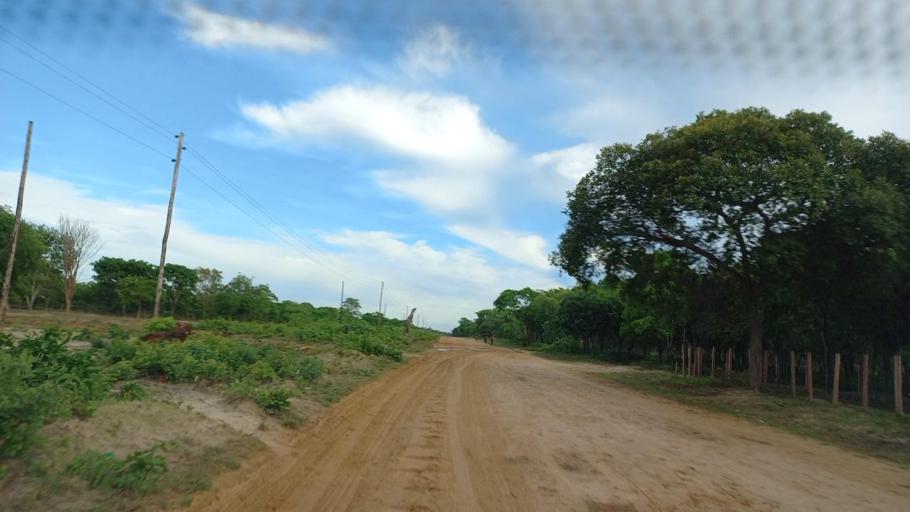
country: ZM
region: North-Western
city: Kabompo
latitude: -13.4131
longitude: 24.3172
